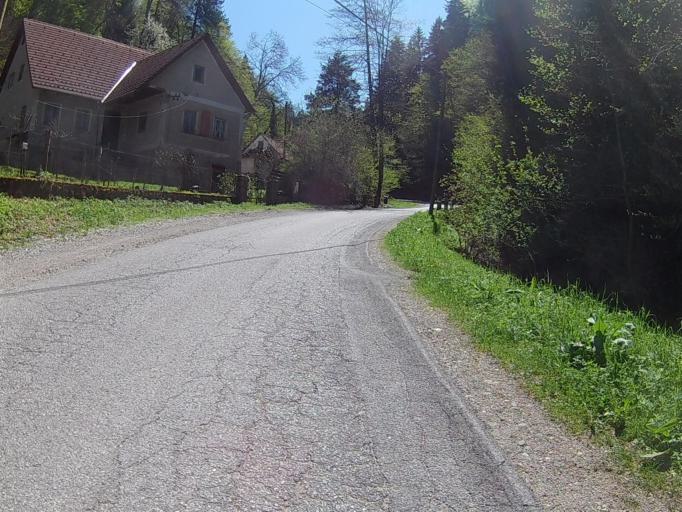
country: SI
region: Ruse
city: Ruse
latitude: 46.5361
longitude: 15.5161
